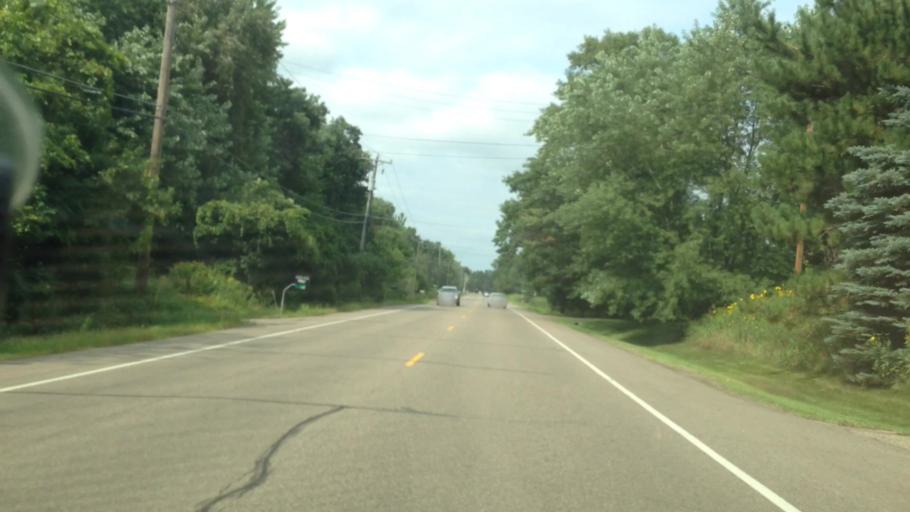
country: US
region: Minnesota
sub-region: Anoka County
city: Circle Pines
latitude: 45.1302
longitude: -93.1273
